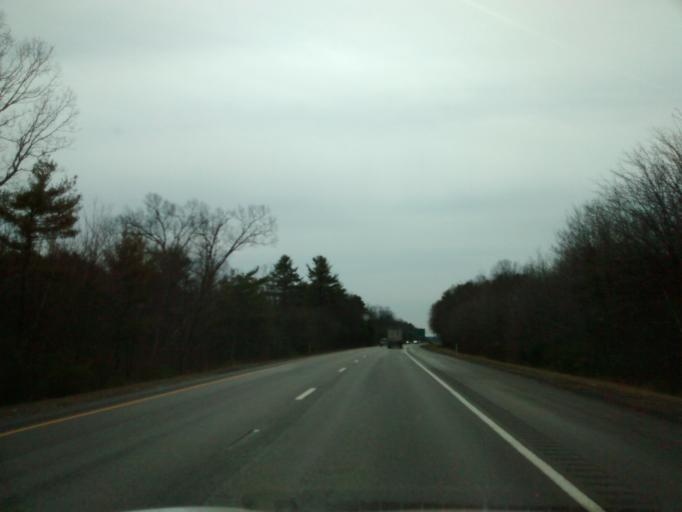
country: US
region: Massachusetts
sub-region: Worcester County
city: Oxford
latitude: 42.1384
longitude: -71.8567
